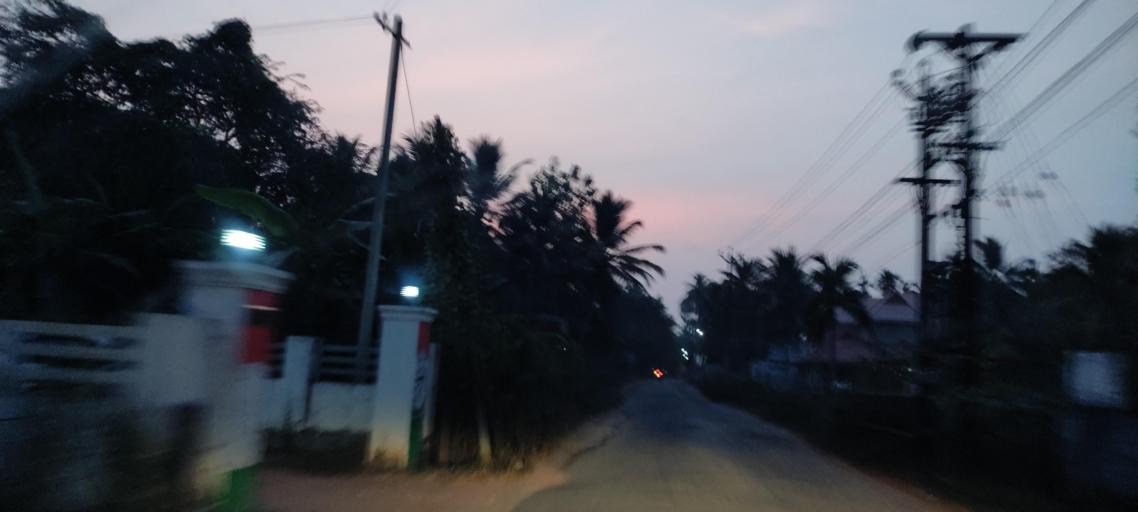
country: IN
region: Kerala
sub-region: Alappuzha
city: Mavelikara
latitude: 9.3213
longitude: 76.4503
